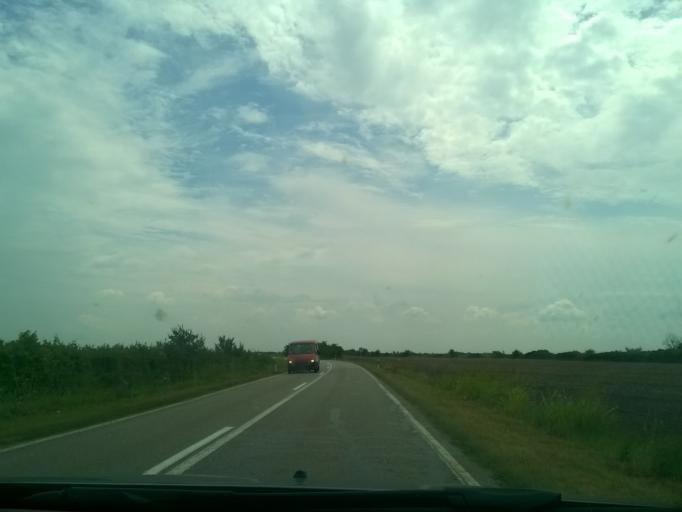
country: RS
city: Konak
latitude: 45.3021
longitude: 20.9220
